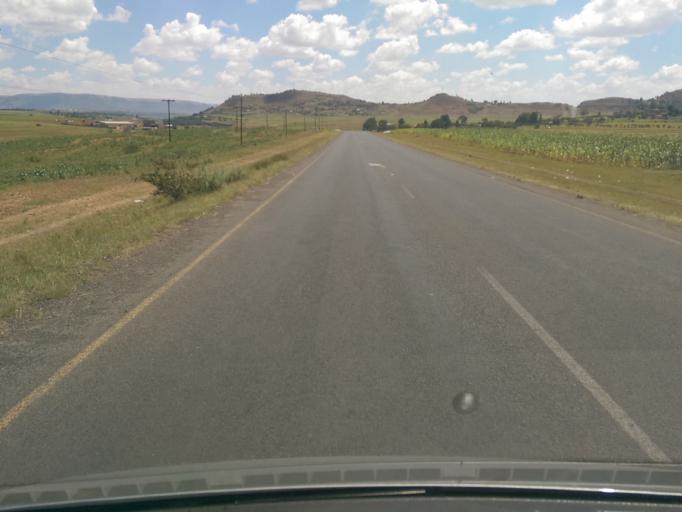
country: LS
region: Maseru
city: Maseru
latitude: -29.4200
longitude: 27.6543
